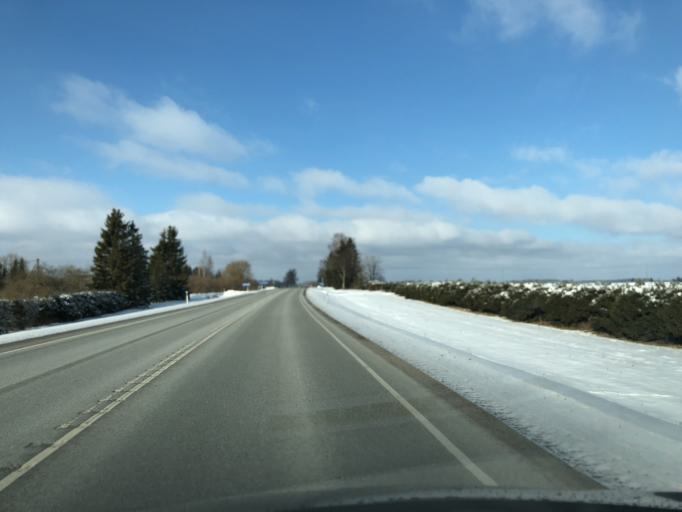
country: EE
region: Jaervamaa
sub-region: Paide linn
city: Paide
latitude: 58.8510
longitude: 25.7273
